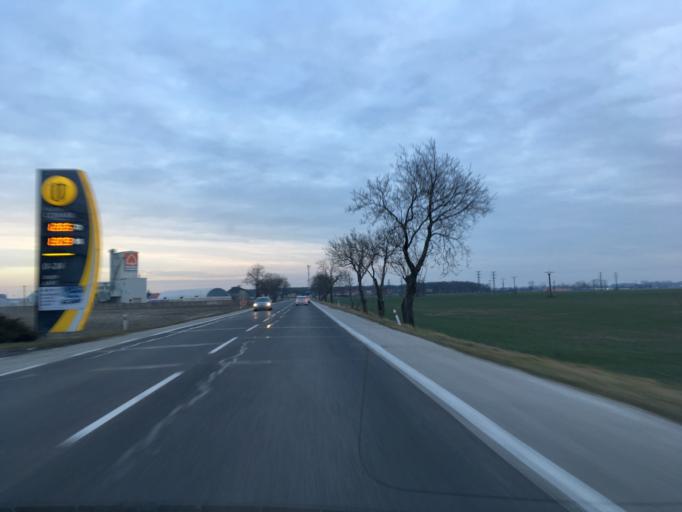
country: SK
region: Trnavsky
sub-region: Okres Dunajska Streda
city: Velky Meder
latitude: 47.8690
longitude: 17.7576
